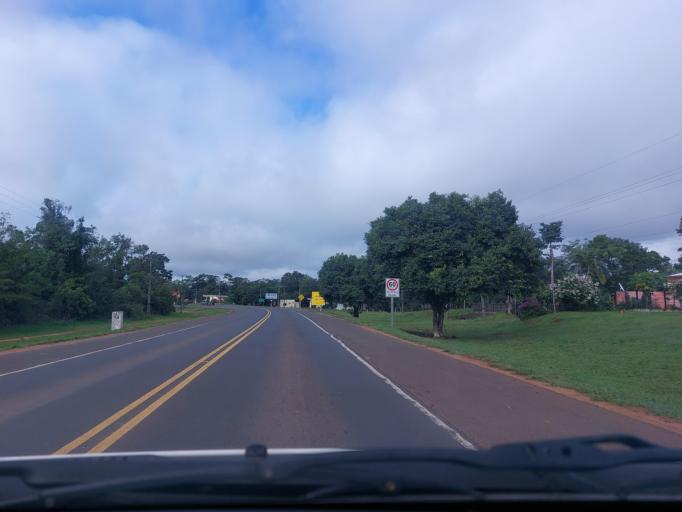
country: PY
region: San Pedro
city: Guayaybi
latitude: -24.5824
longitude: -56.4021
